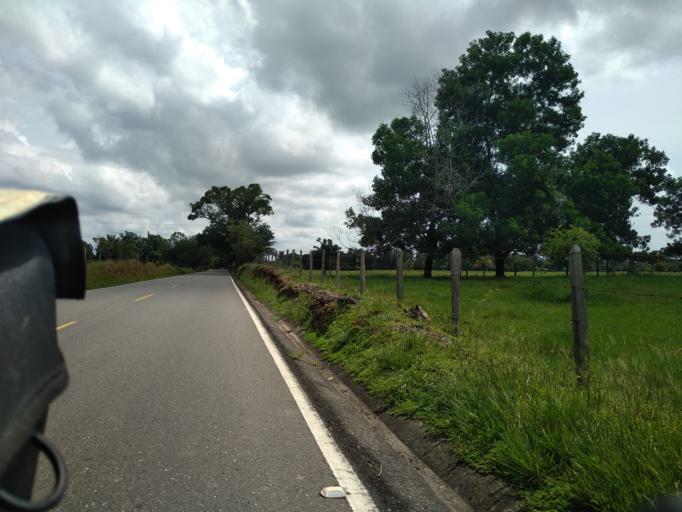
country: CO
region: Santander
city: Cimitarra
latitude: 6.4615
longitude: -74.0281
